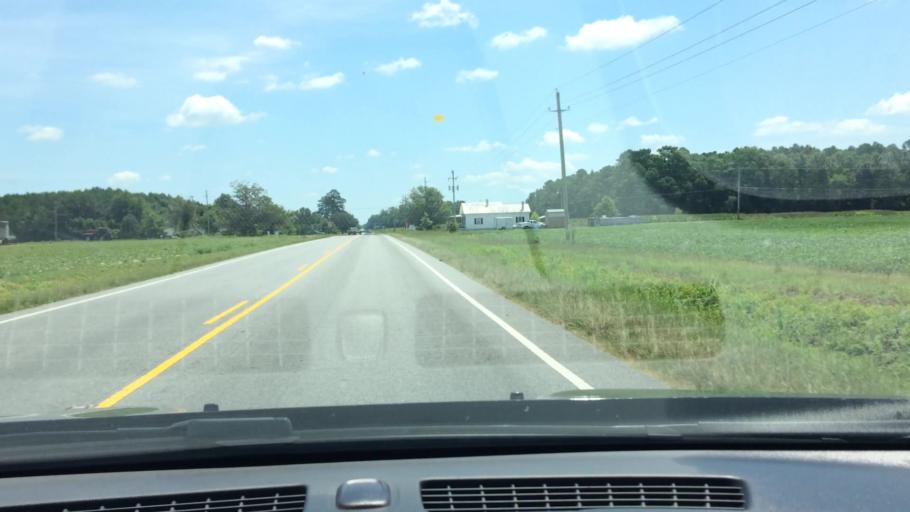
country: US
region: North Carolina
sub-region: Pitt County
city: Ayden
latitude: 35.4713
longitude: -77.3871
